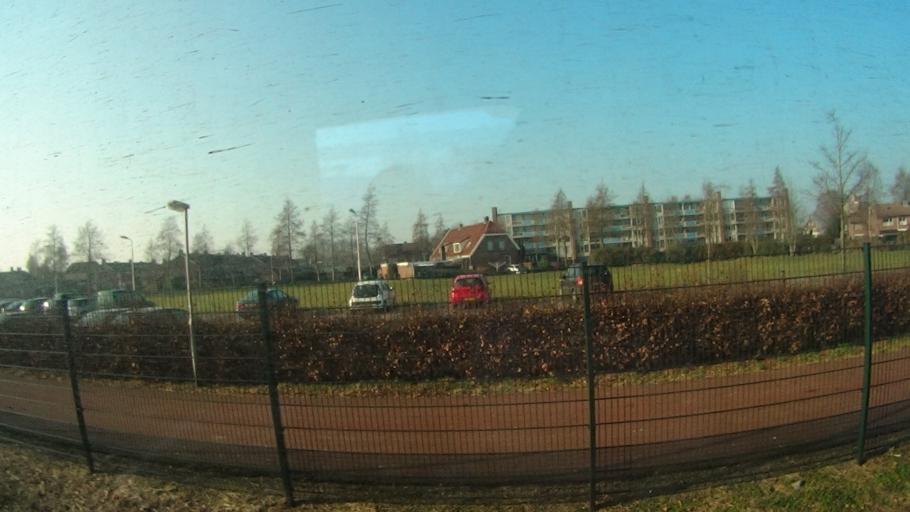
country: NL
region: Overijssel
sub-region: Gemeente Hardenberg
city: Hardenberg
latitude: 52.5735
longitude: 6.6294
